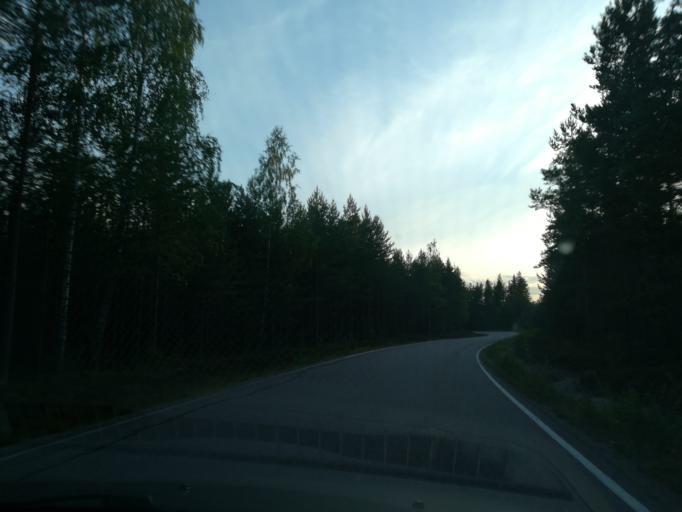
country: FI
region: South Karelia
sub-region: Lappeenranta
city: Joutseno
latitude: 61.3460
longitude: 28.4256
